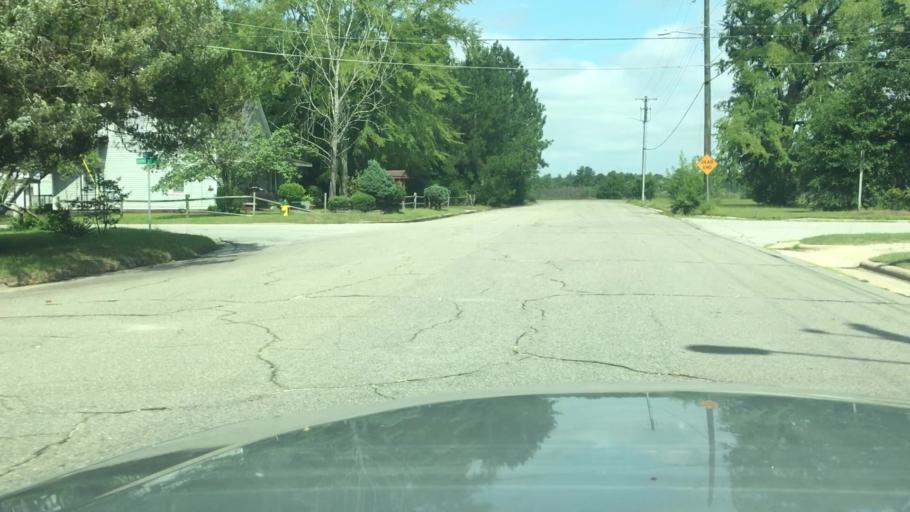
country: US
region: North Carolina
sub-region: Cumberland County
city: Fayetteville
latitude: 35.0253
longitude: -78.9026
